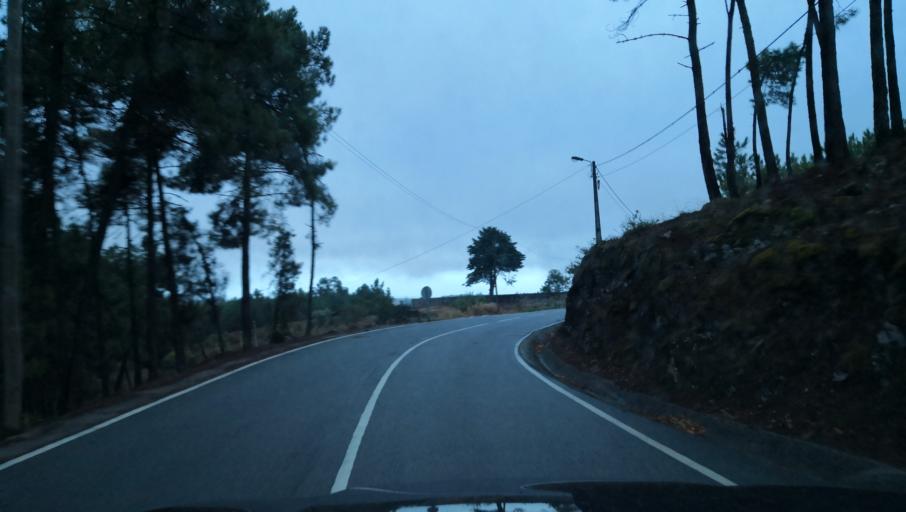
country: PT
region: Vila Real
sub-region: Sabrosa
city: Sabrosa
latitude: 41.2891
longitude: -7.5777
